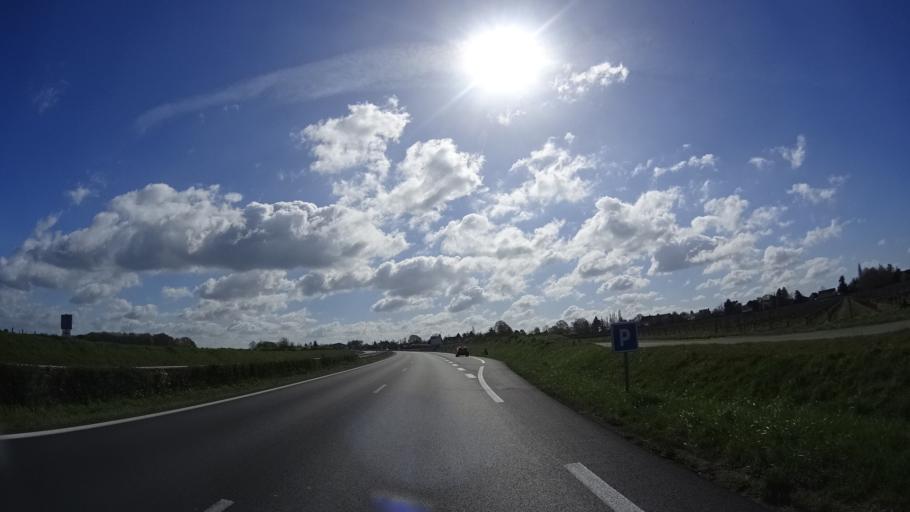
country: FR
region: Pays de la Loire
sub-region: Departement de Maine-et-Loire
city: Saint-Melaine-sur-Aubance
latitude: 47.3900
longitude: -0.4993
